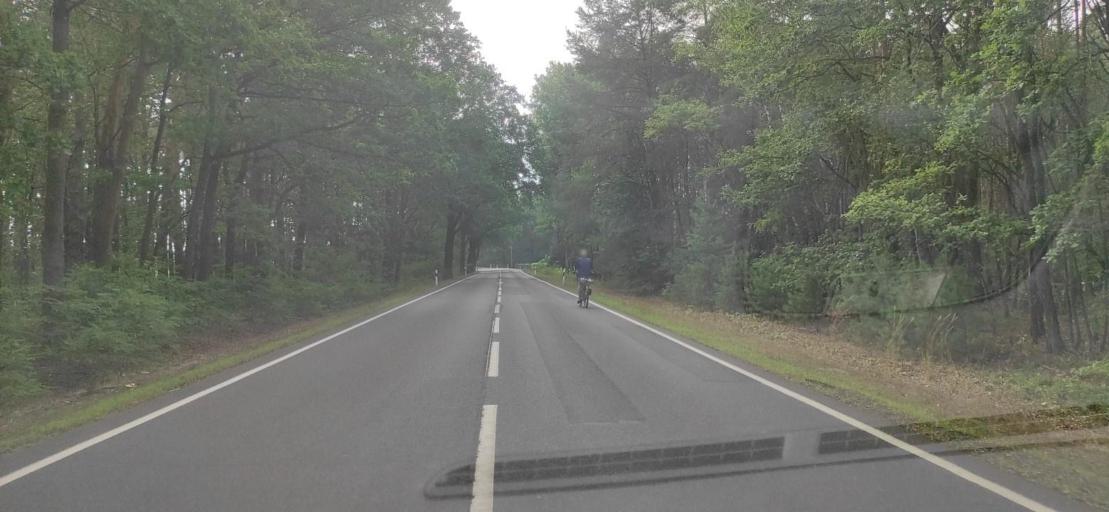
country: DE
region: Brandenburg
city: Forst
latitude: 51.7087
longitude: 14.6761
